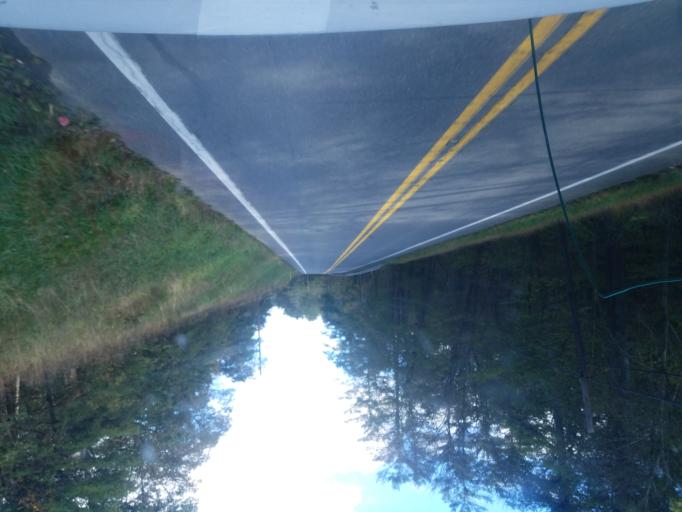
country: US
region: Pennsylvania
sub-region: Fulton County
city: McConnellsburg
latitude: 39.9888
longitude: -78.0668
